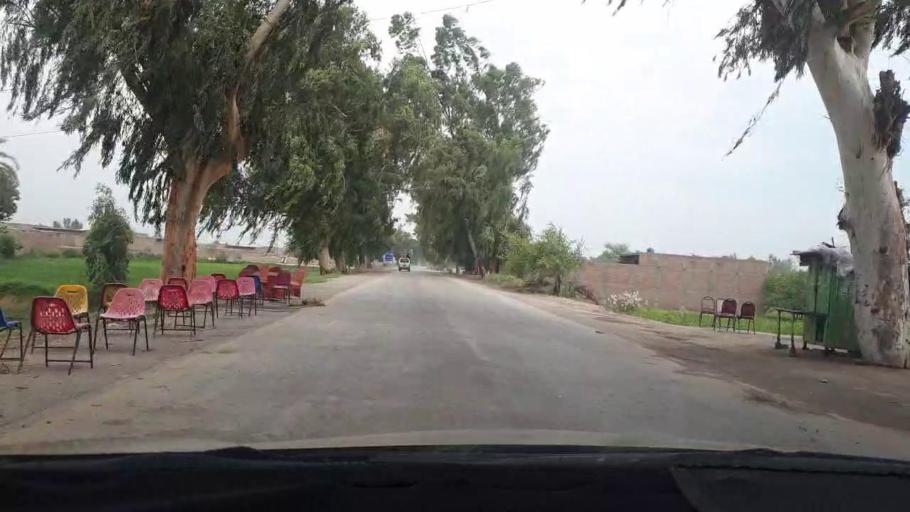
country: PK
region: Sindh
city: Naudero
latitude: 27.6590
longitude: 68.3450
